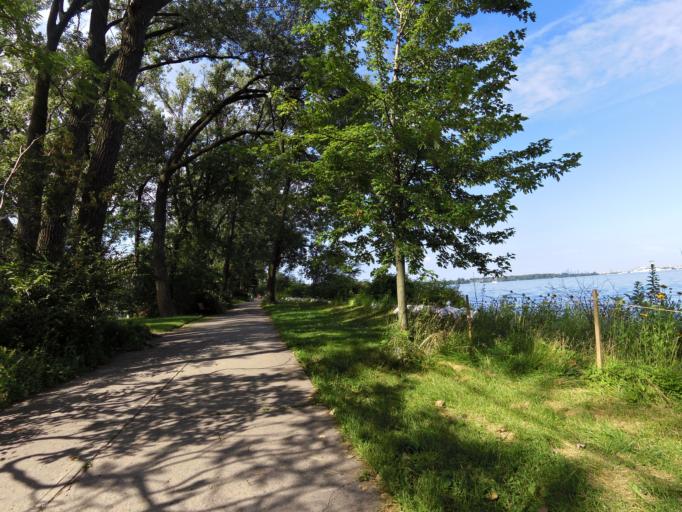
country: CA
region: Ontario
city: Toronto
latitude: 43.6288
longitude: -79.3603
